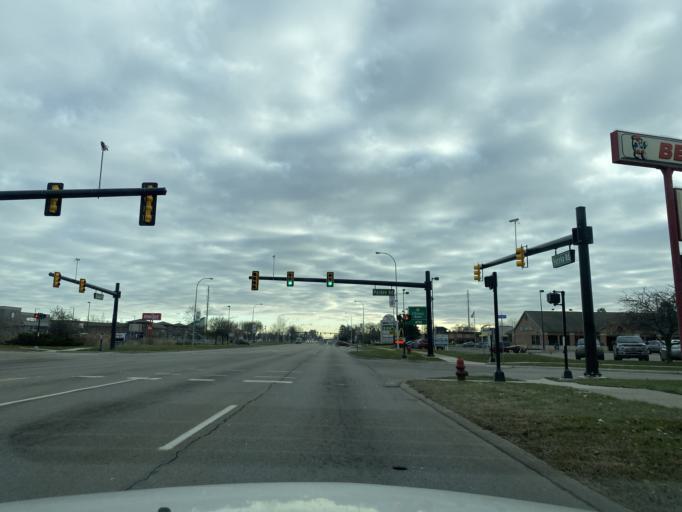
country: US
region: Michigan
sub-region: Wayne County
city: Taylor
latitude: 42.1976
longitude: -83.2620
